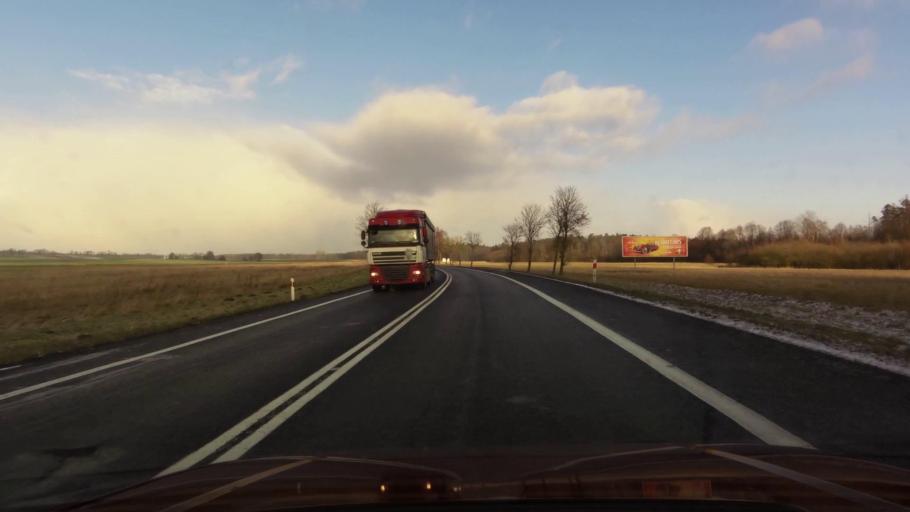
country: PL
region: West Pomeranian Voivodeship
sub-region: Powiat bialogardzki
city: Bialogard
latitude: 54.0820
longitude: 15.9805
